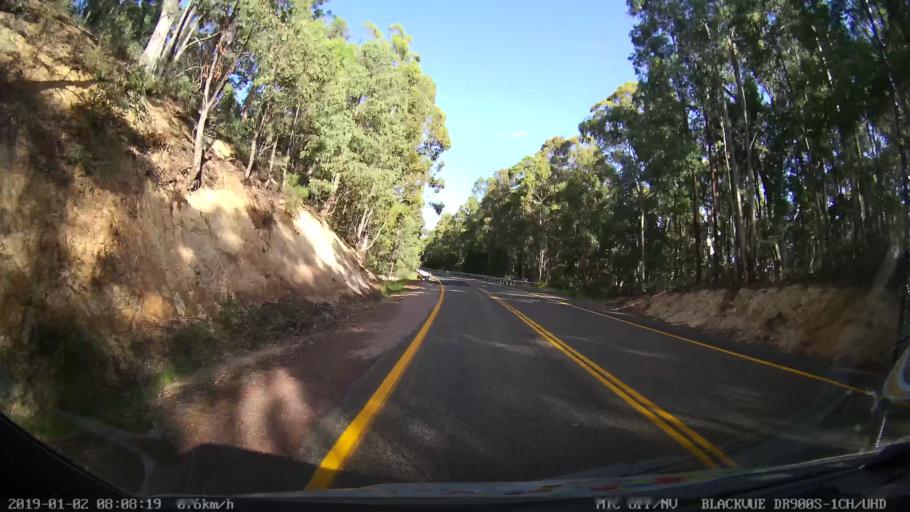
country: AU
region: New South Wales
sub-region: Tumut Shire
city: Tumut
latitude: -35.6171
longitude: 148.3869
